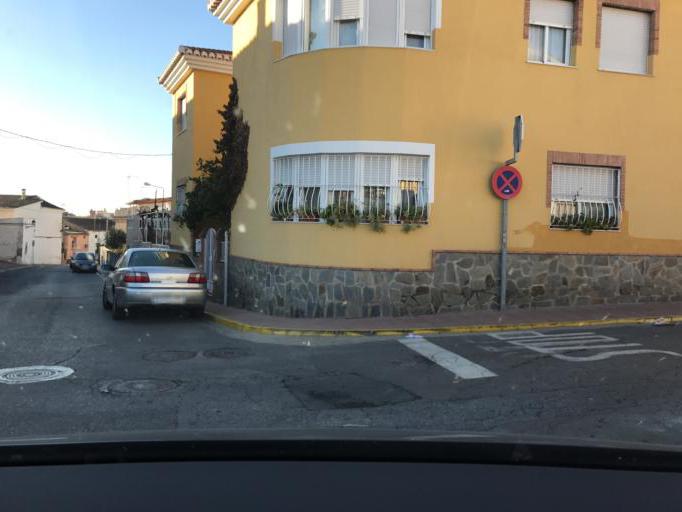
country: ES
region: Andalusia
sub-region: Provincia de Granada
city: Peligros
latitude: 37.2344
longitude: -3.6256
